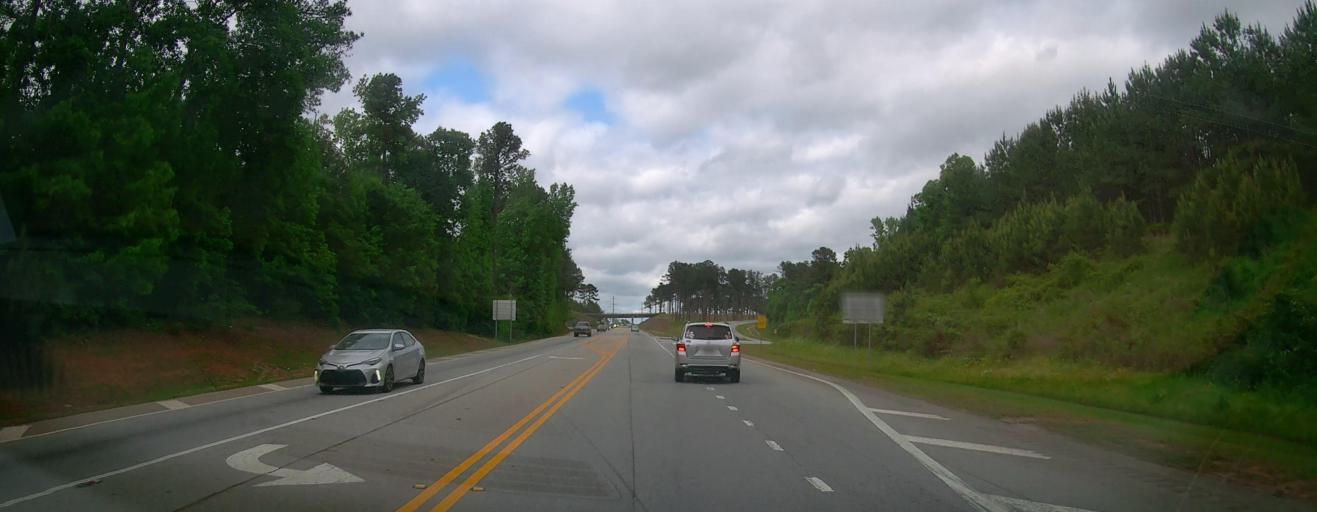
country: US
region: Georgia
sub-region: Walton County
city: Monroe
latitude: 33.7987
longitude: -83.7397
